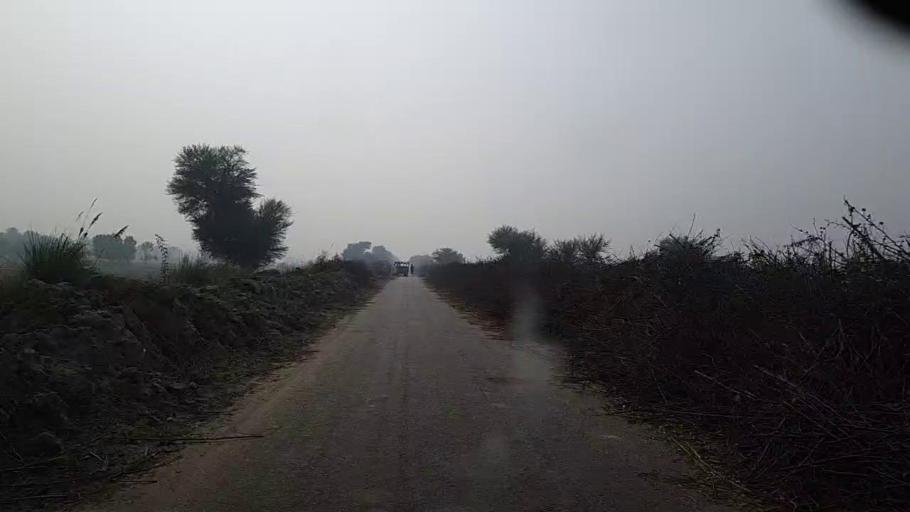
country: PK
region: Sindh
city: Kandiari
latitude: 26.9919
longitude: 68.6049
